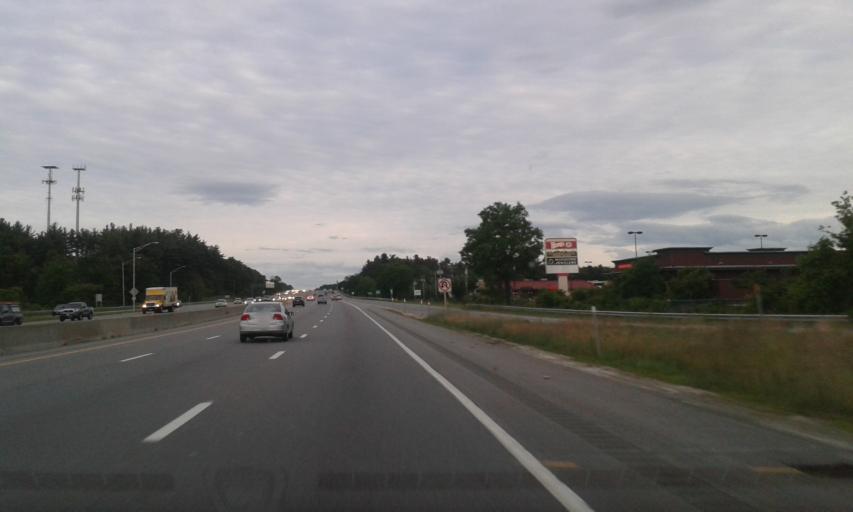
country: US
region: New Hampshire
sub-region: Hillsborough County
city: Nashua
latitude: 42.7678
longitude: -71.4936
